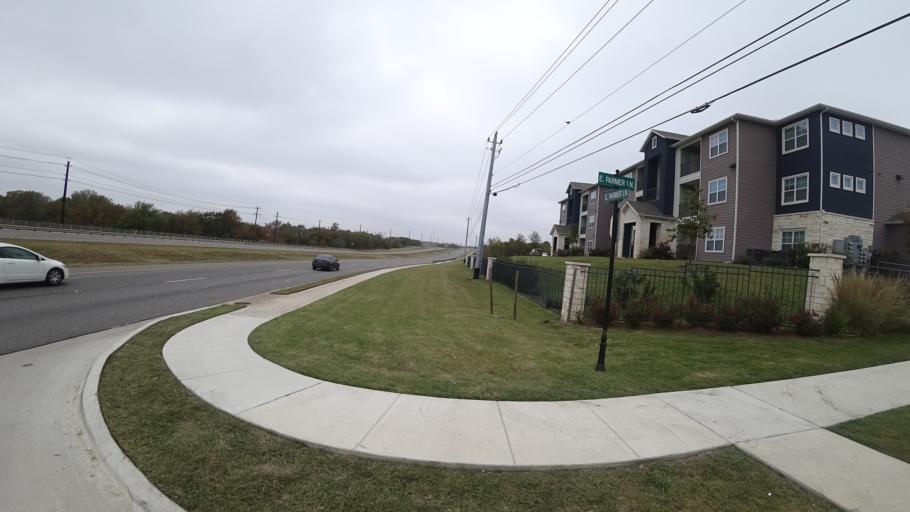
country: US
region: Texas
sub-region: Travis County
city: Pflugerville
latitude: 30.3903
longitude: -97.6522
